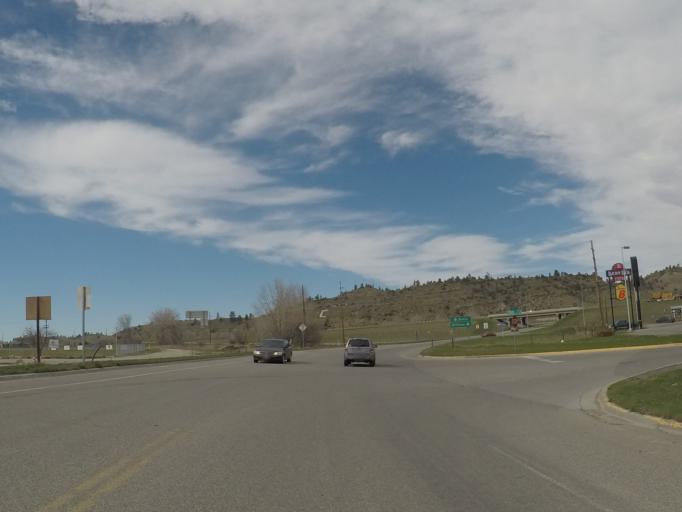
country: US
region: Montana
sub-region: Stillwater County
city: Columbus
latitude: 45.6443
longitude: -109.2485
